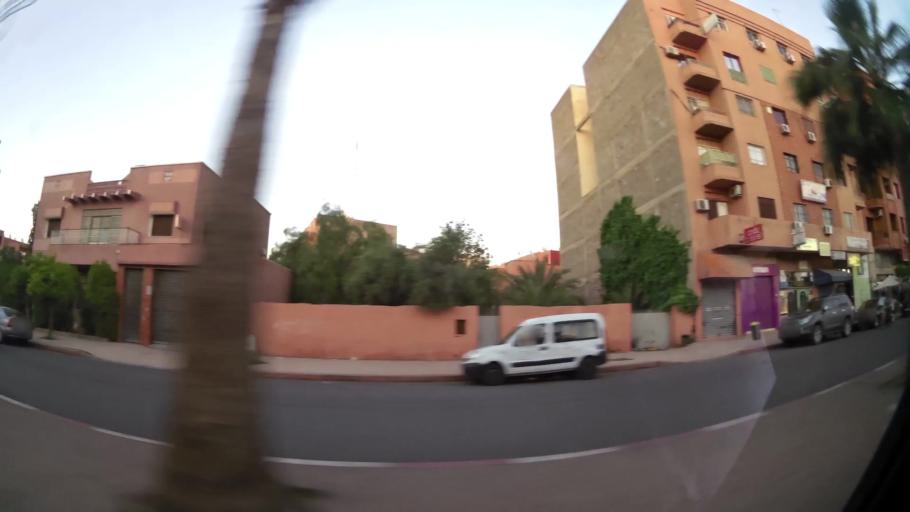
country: MA
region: Marrakech-Tensift-Al Haouz
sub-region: Marrakech
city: Marrakesh
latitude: 31.6415
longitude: -8.0001
